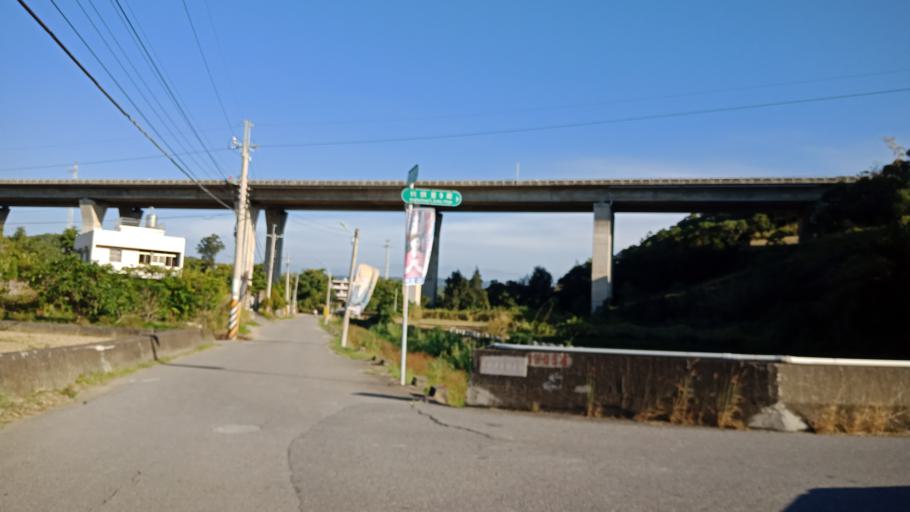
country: TW
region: Taiwan
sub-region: Miaoli
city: Miaoli
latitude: 24.4852
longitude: 120.6991
